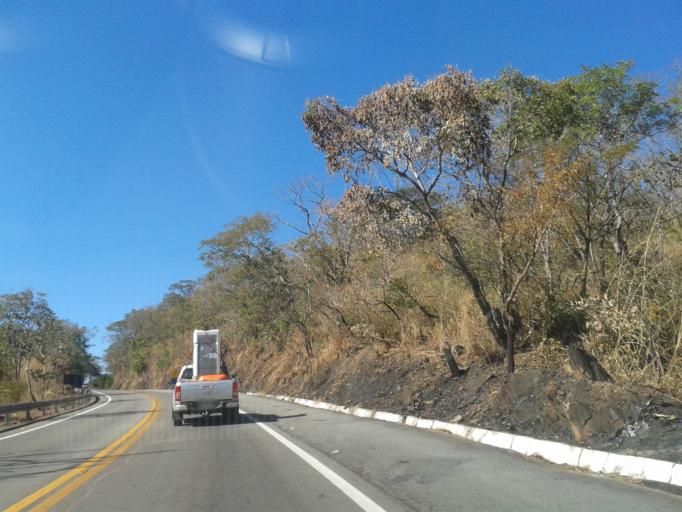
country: BR
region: Goias
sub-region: Goias
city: Goias
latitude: -15.9255
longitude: -50.1375
